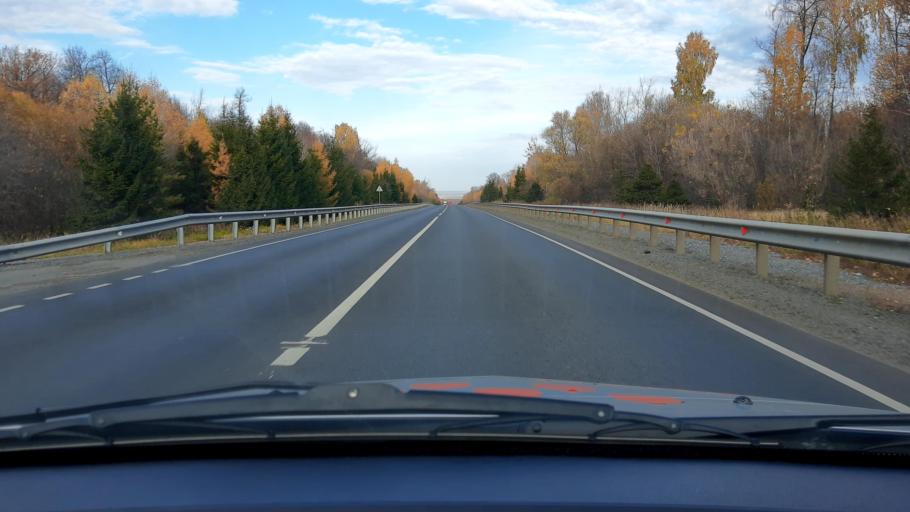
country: RU
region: Bashkortostan
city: Avdon
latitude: 54.8366
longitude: 55.7212
